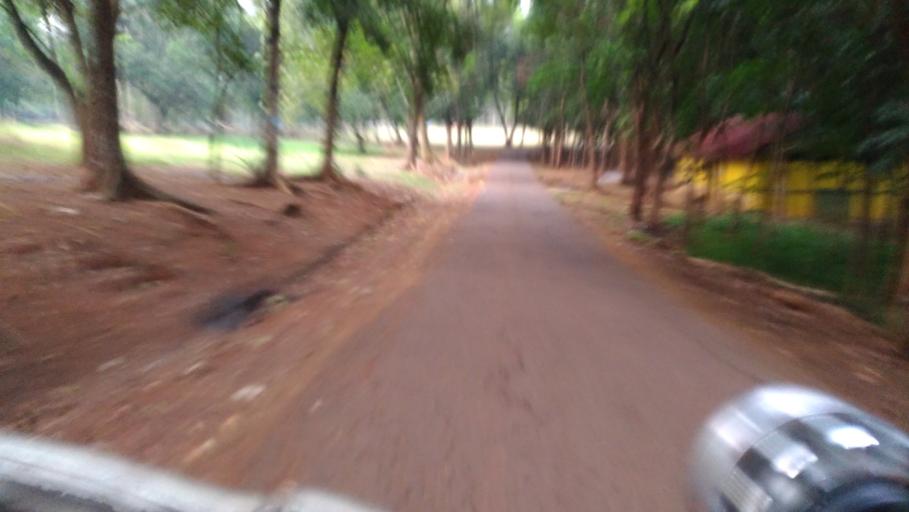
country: ID
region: West Java
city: Cileungsir
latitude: -6.3605
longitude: 106.9004
